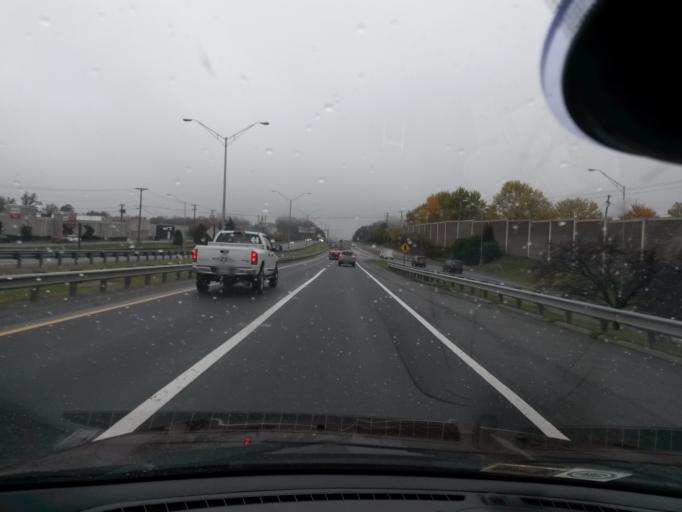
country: US
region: Virginia
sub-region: Montgomery County
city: Christiansburg
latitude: 37.1345
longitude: -80.3751
